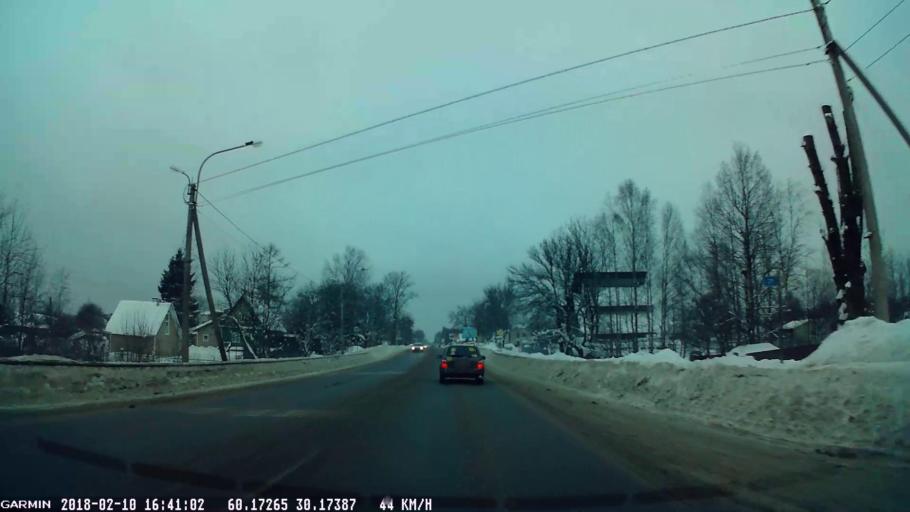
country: RU
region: Leningrad
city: Sertolovo
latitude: 60.1628
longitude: 30.1829
